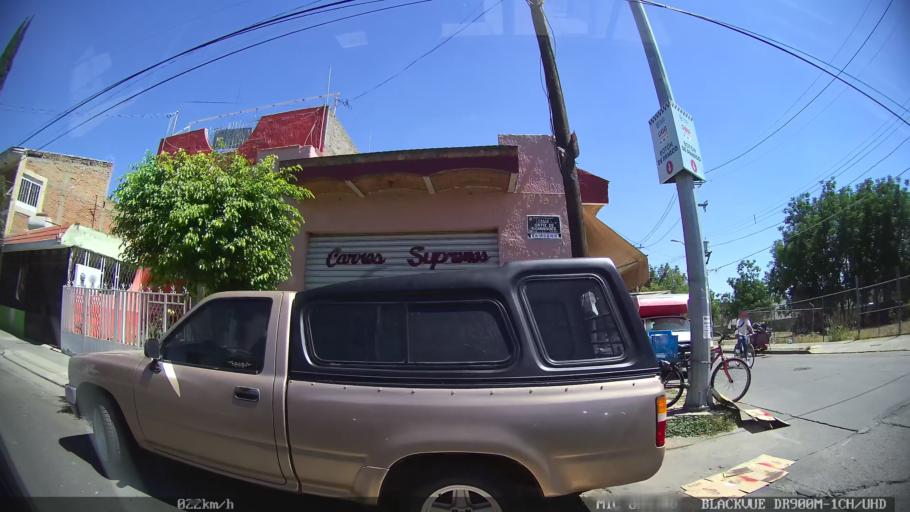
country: MX
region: Jalisco
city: Tlaquepaque
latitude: 20.6666
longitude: -103.2853
